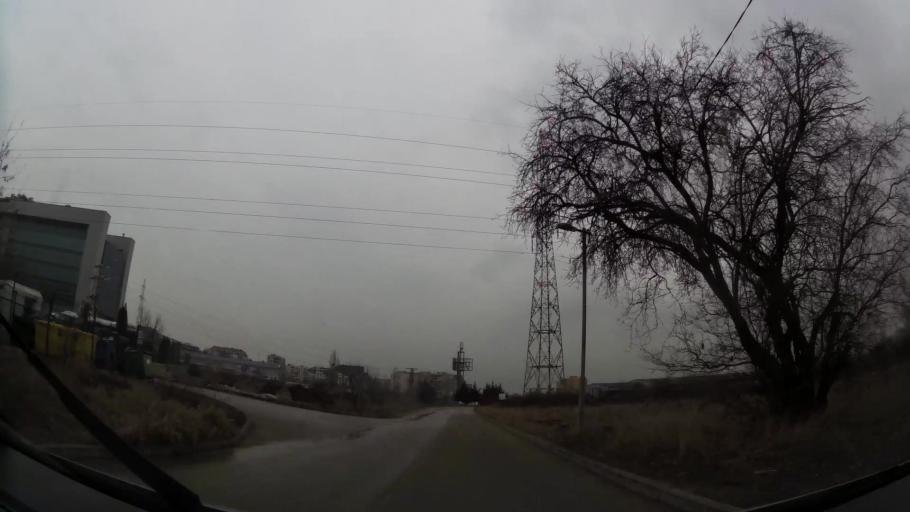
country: BG
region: Sofia-Capital
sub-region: Stolichna Obshtina
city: Sofia
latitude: 42.6214
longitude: 23.3818
